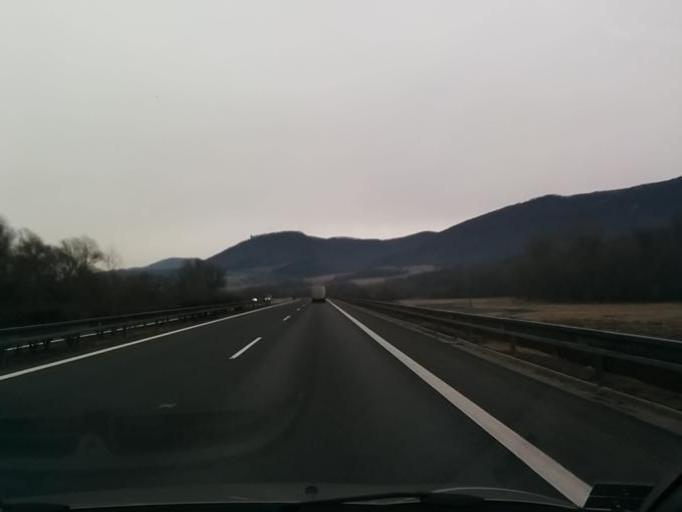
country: SK
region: Banskobystricky
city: Nova Bana
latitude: 48.3721
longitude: 18.5986
